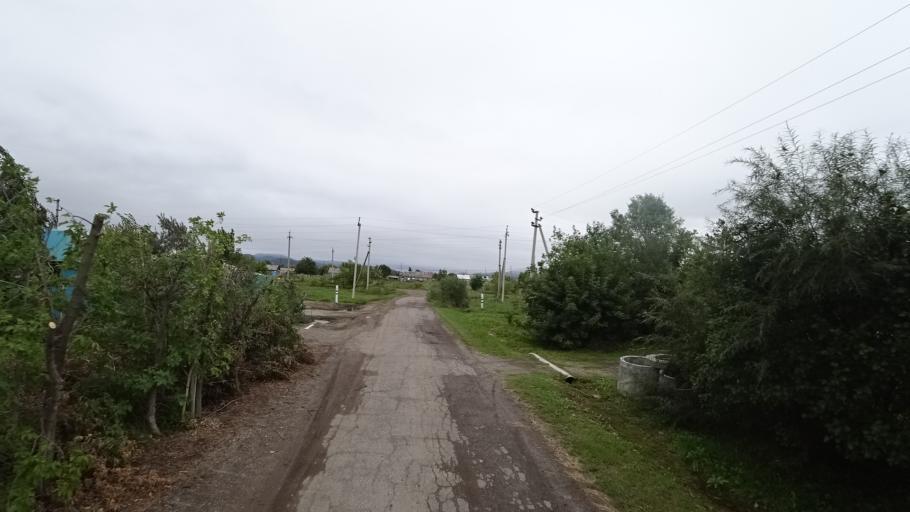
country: RU
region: Primorskiy
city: Chernigovka
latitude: 44.3266
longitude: 132.5999
